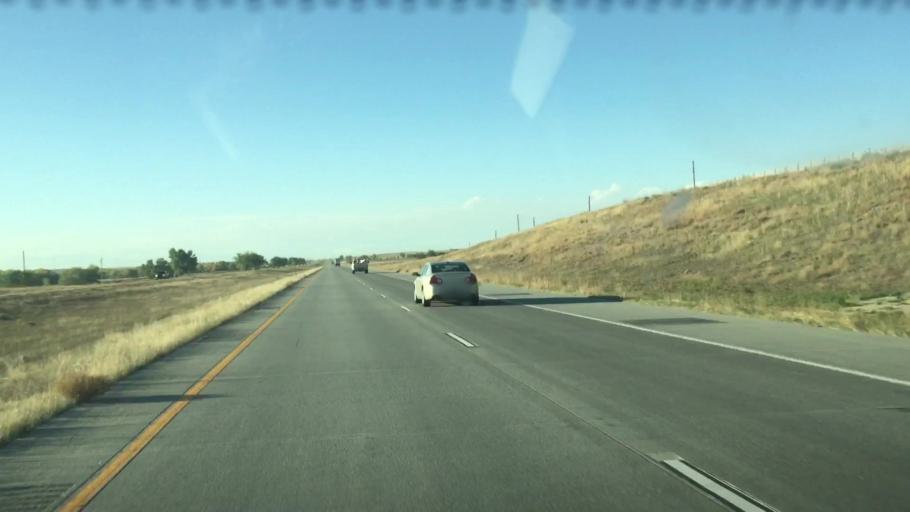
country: US
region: Colorado
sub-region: Arapahoe County
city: Byers
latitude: 39.5540
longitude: -104.0056
